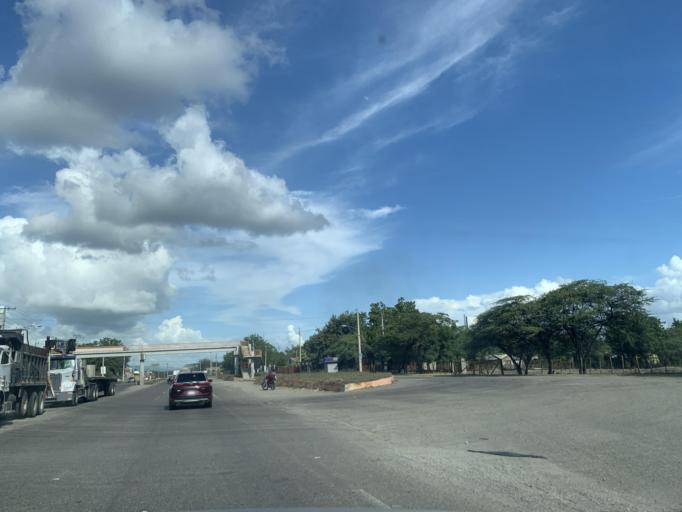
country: DO
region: Santiago
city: Villa Gonzalez
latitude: 19.5529
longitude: -70.8205
